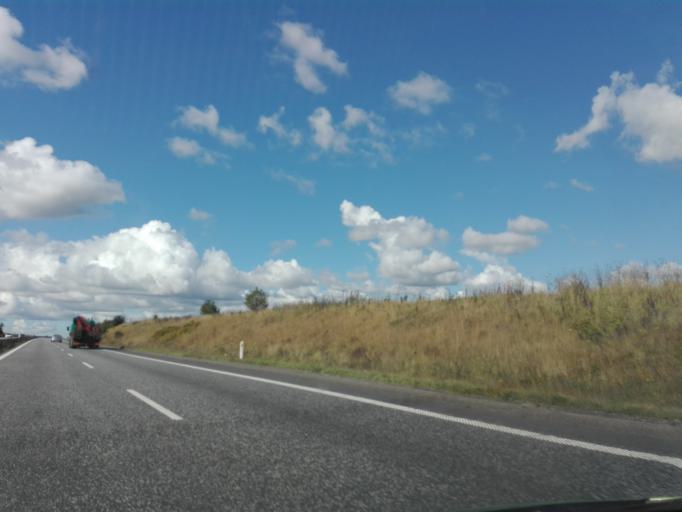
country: DK
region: Central Jutland
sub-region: Randers Kommune
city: Spentrup
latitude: 56.5260
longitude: 9.9426
